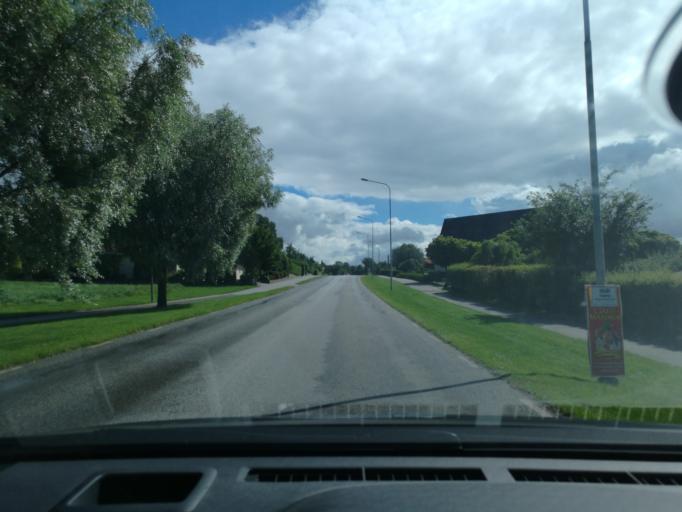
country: SE
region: Skane
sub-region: Eslovs Kommun
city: Eslov
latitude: 55.8290
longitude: 13.2908
